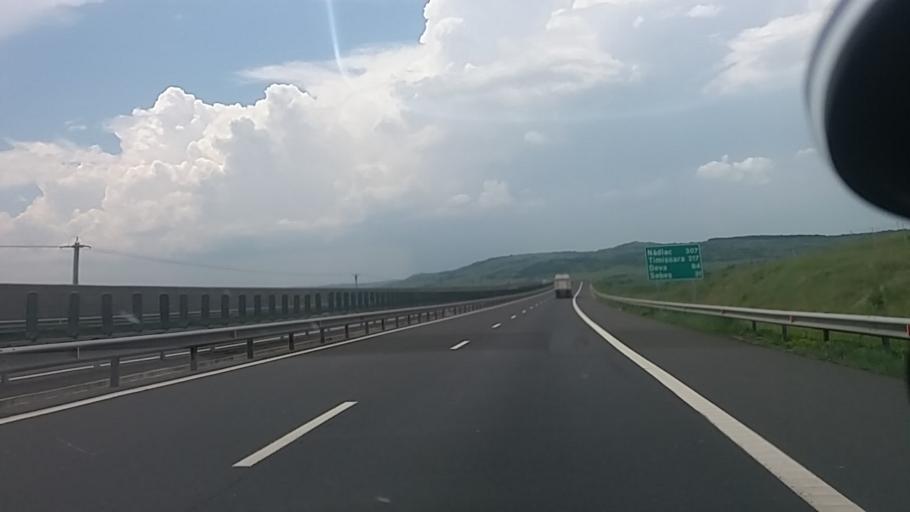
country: RO
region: Sibiu
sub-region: Comuna Apoldu de Jos
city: Apoldu de Jos
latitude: 45.8806
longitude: 23.8581
